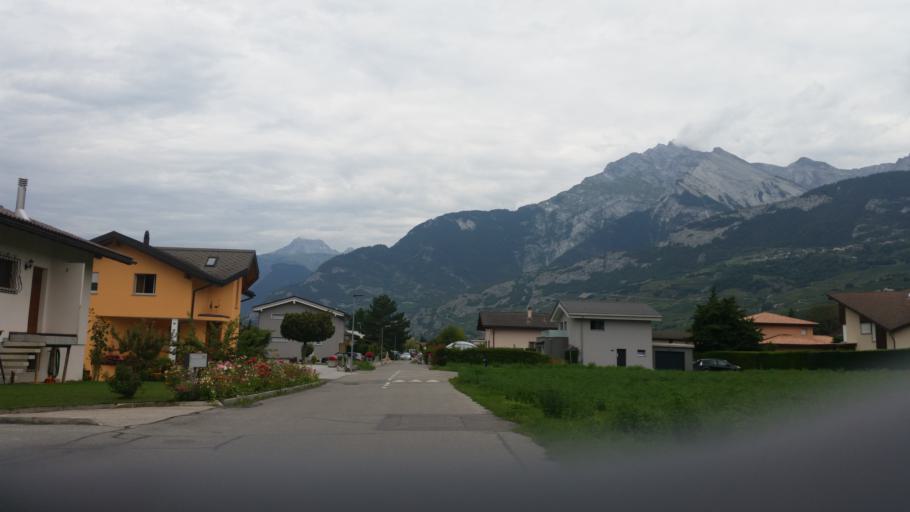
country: CH
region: Valais
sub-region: Conthey District
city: Conthey
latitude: 46.2261
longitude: 7.3105
